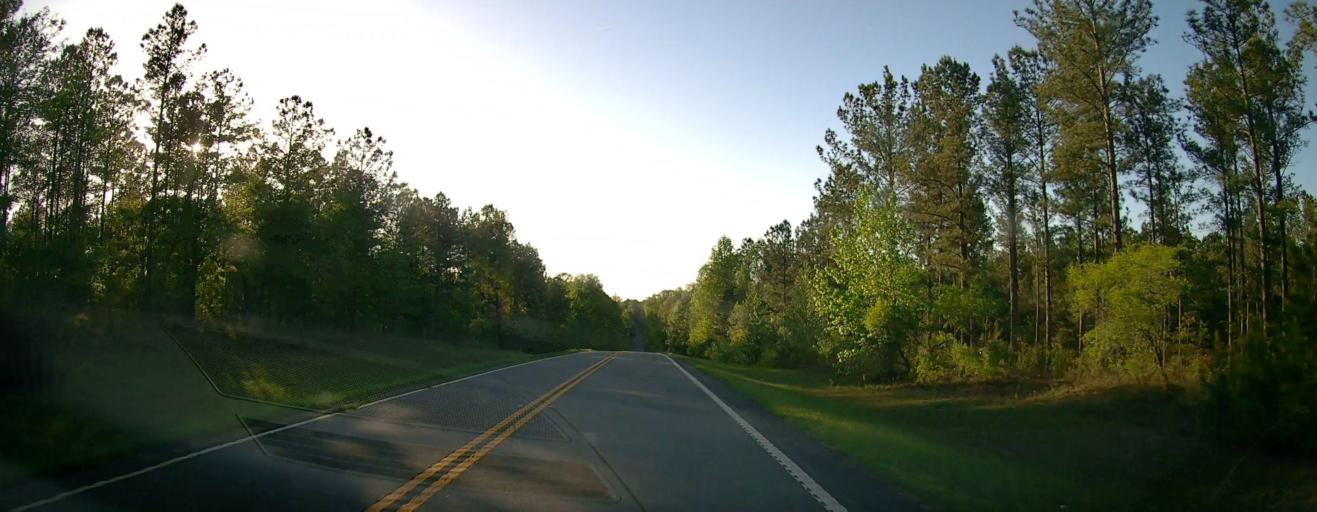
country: US
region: Georgia
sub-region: Schley County
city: Ellaville
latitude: 32.3513
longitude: -84.3796
